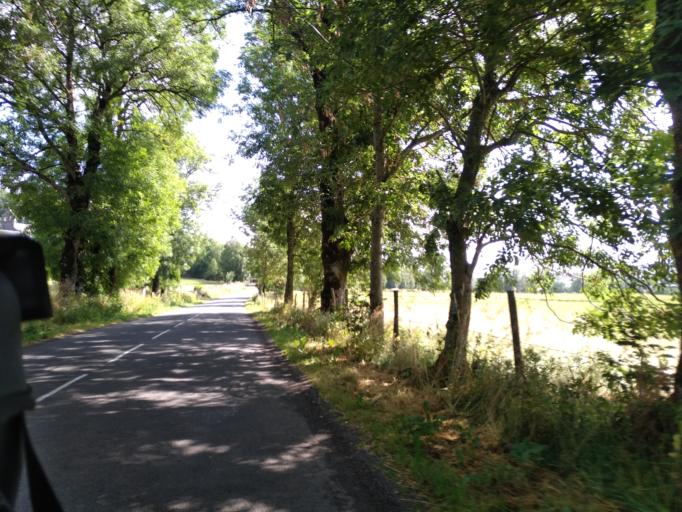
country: FR
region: Auvergne
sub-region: Departement du Cantal
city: Murat
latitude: 45.1560
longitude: 2.7841
